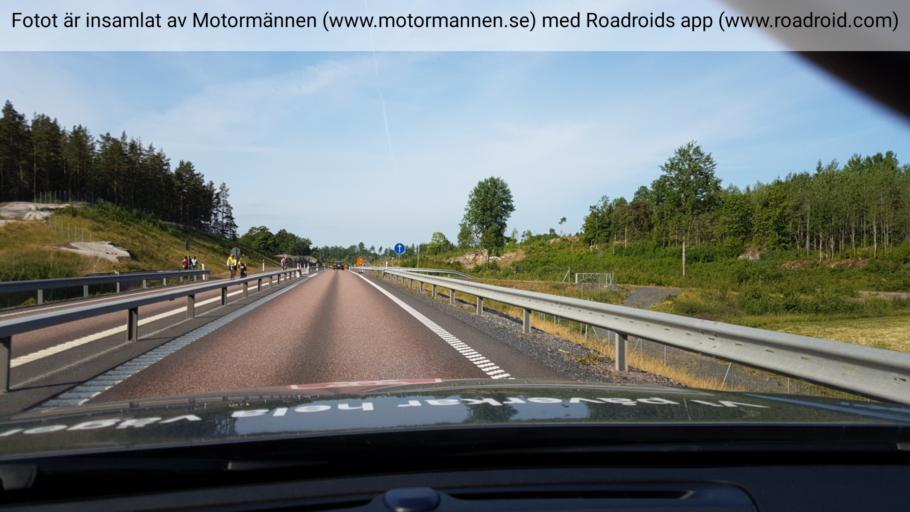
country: SE
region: OErebro
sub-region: Askersunds Kommun
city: Askersund
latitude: 58.8267
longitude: 14.8911
